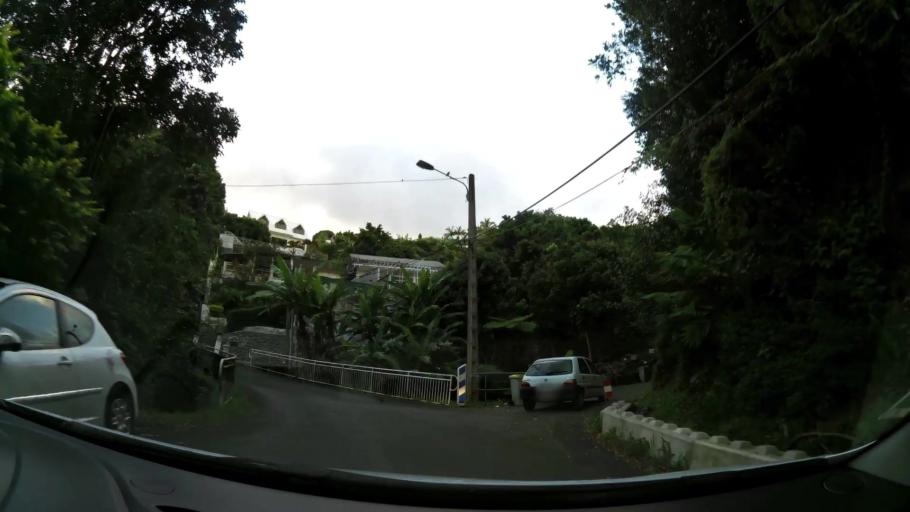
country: RE
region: Reunion
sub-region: Reunion
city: Saint-Denis
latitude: -20.9204
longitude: 55.4630
